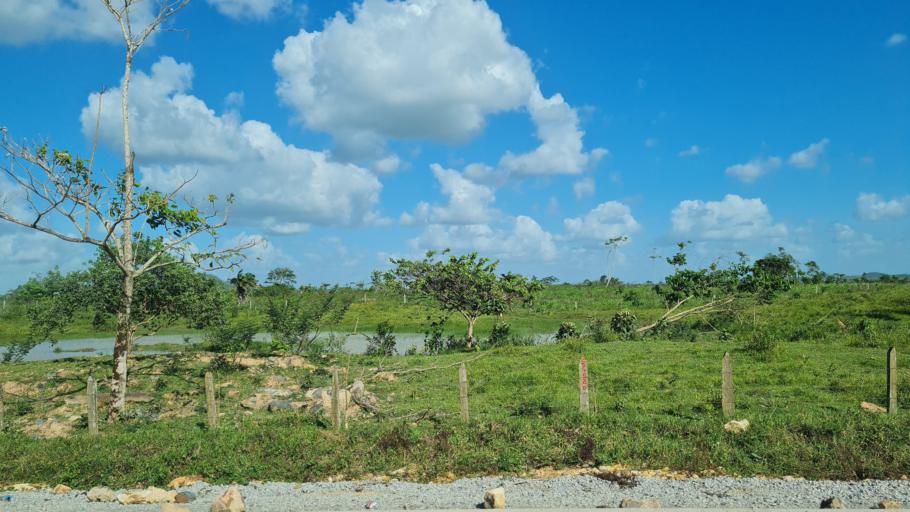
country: NI
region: Atlantico Norte (RAAN)
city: Bonanza
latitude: 13.9983
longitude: -84.1666
